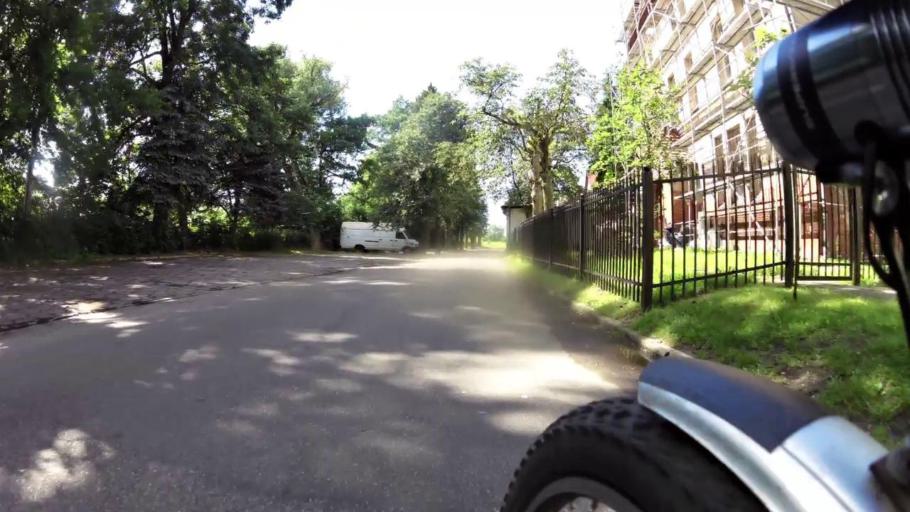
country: PL
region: West Pomeranian Voivodeship
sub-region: Powiat bialogardzki
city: Bialogard
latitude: 54.0027
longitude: 15.9801
